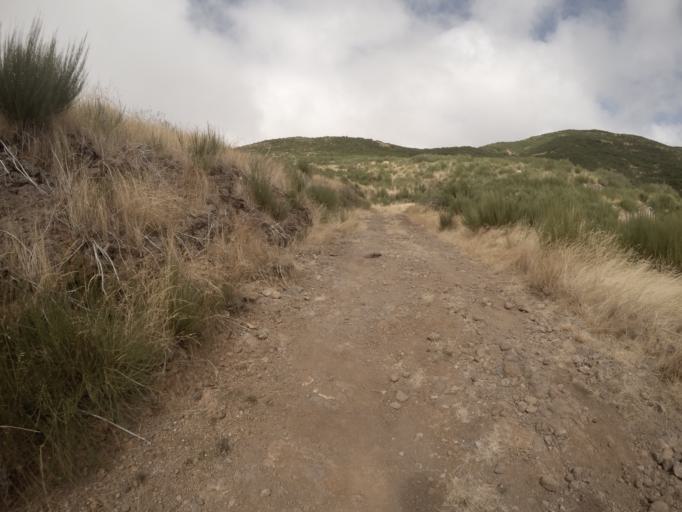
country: PT
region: Madeira
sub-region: Camara de Lobos
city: Curral das Freiras
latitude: 32.7119
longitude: -16.9968
